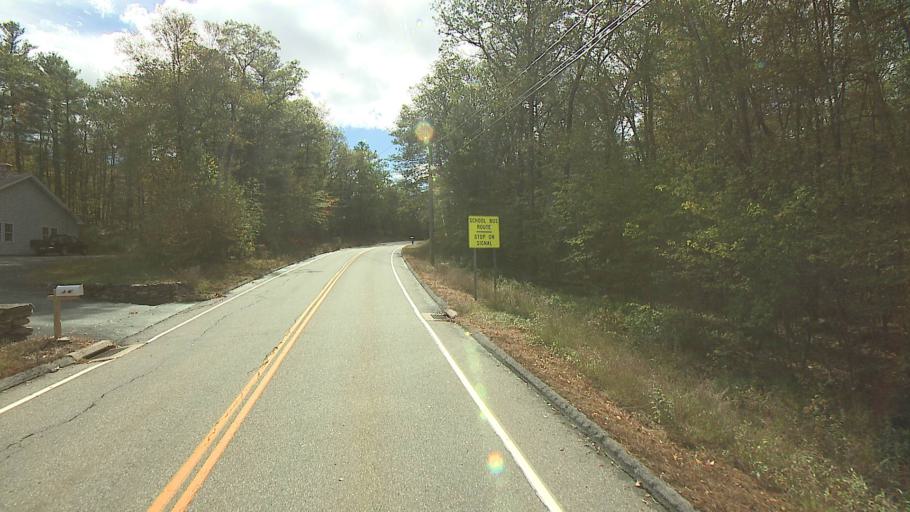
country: US
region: Massachusetts
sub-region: Worcester County
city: Webster
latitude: 42.0229
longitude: -71.8875
